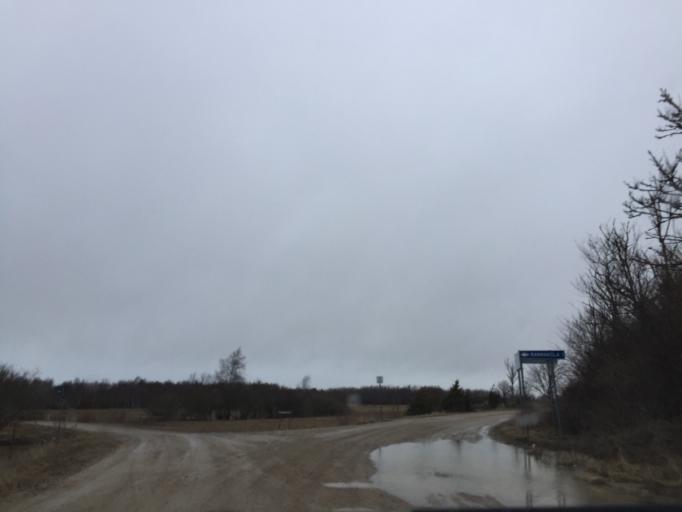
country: EE
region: Laeaene
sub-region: Haapsalu linn
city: Haapsalu
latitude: 58.6780
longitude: 23.5416
